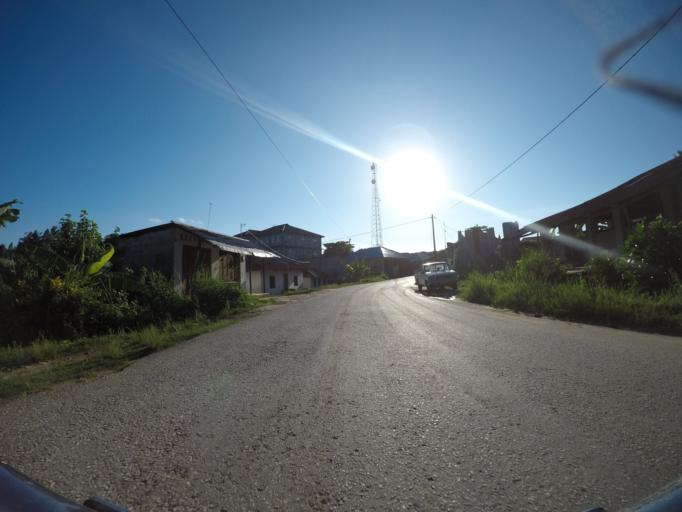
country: TZ
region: Pemba South
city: Mtambile
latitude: -5.3777
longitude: 39.7028
